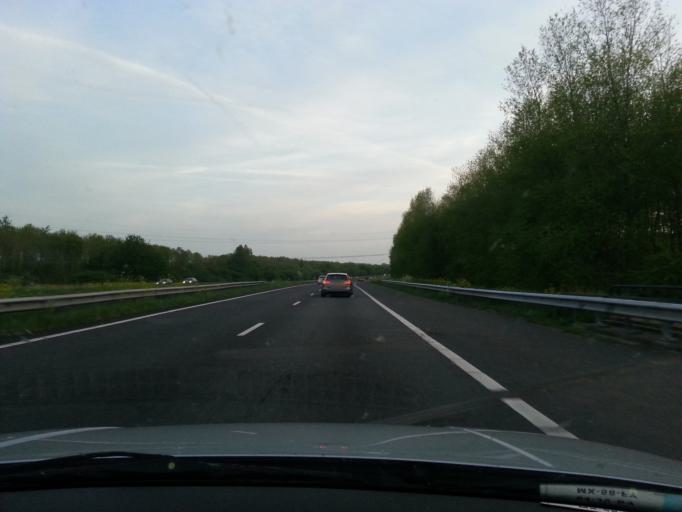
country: NL
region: Flevoland
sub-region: Gemeente Lelystad
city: Lelystad
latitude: 52.4999
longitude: 5.5296
